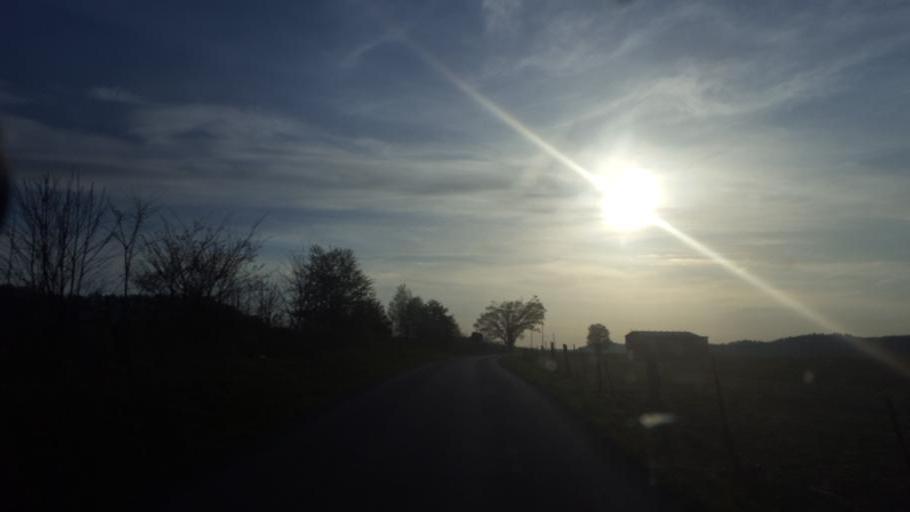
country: US
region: Kentucky
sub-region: Hart County
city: Horse Cave
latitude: 37.2234
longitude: -85.9477
